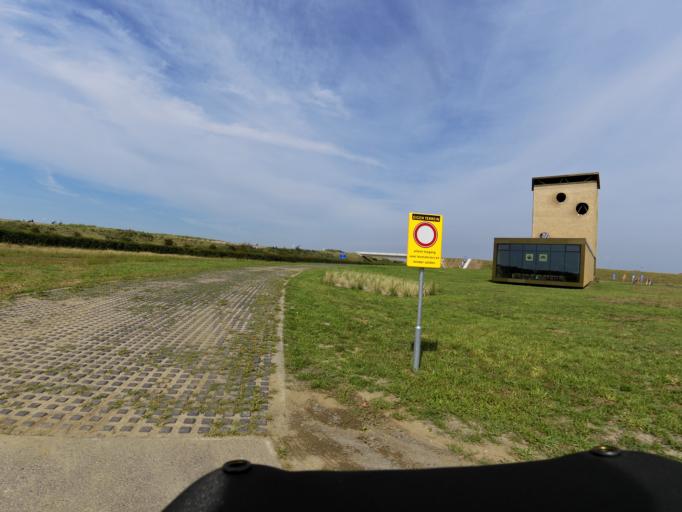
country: NL
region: Zeeland
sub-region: Schouwen-Duiveland
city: Scharendijke
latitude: 51.7580
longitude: 3.8475
